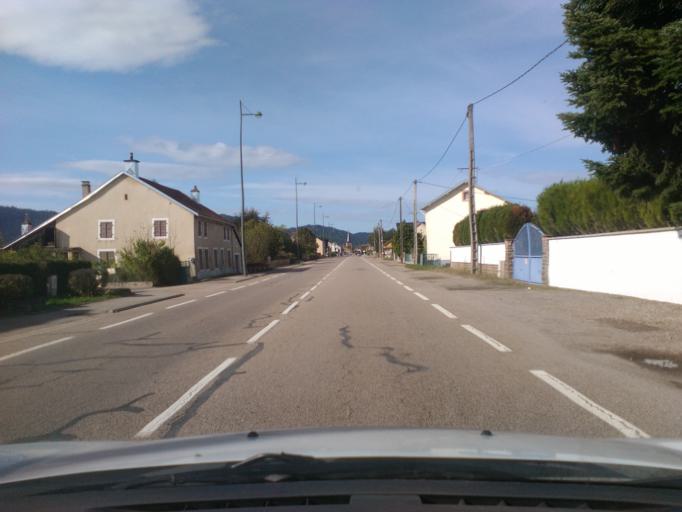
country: FR
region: Lorraine
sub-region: Departement des Vosges
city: Sainte-Marguerite
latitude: 48.2657
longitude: 6.9901
